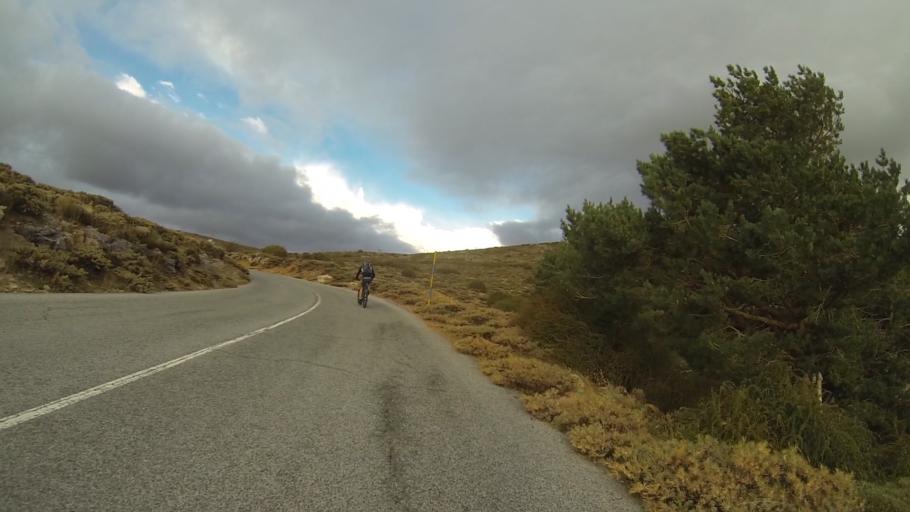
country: ES
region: Andalusia
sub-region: Provincia de Granada
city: Guejar-Sierra
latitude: 37.1201
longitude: -3.4350
